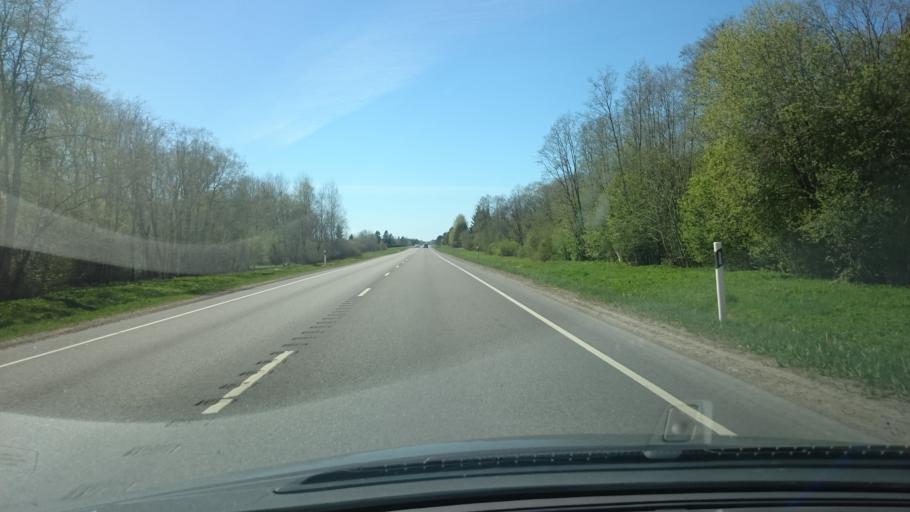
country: EE
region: Ida-Virumaa
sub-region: Sillamaee linn
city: Sillamae
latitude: 59.3917
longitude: 27.7004
